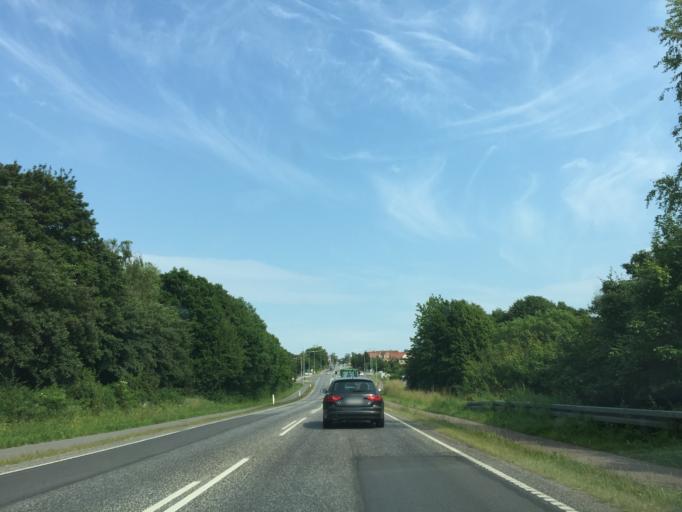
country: DK
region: Central Jutland
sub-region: Syddjurs Kommune
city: Ronde
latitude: 56.3038
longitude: 10.4611
